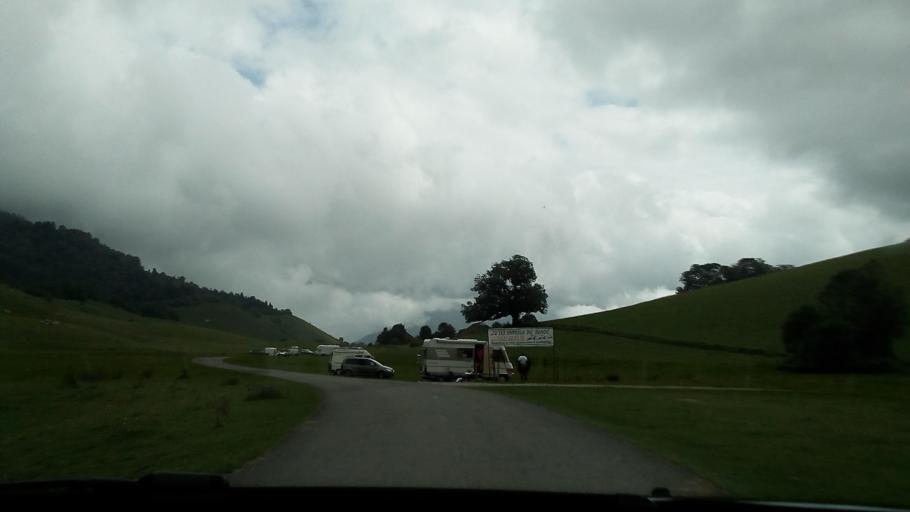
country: FR
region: Aquitaine
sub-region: Departement des Pyrenees-Atlantiques
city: Louvie-Juzon
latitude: 43.0651
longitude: -0.4701
